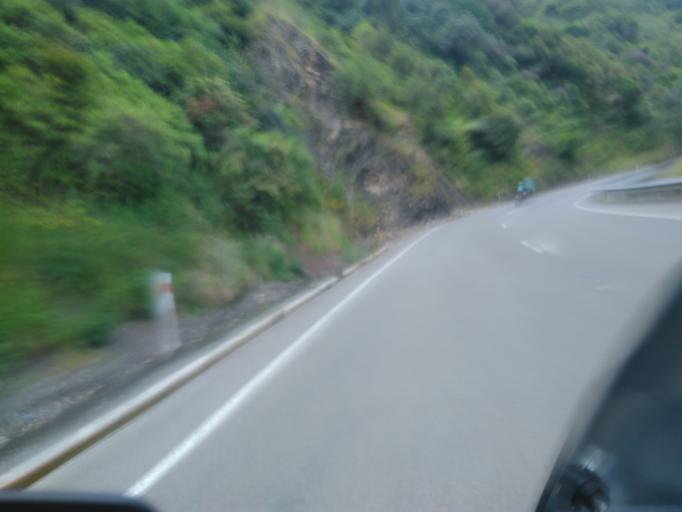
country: NZ
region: Bay of Plenty
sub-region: Opotiki District
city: Opotiki
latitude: -38.2410
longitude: 177.3119
